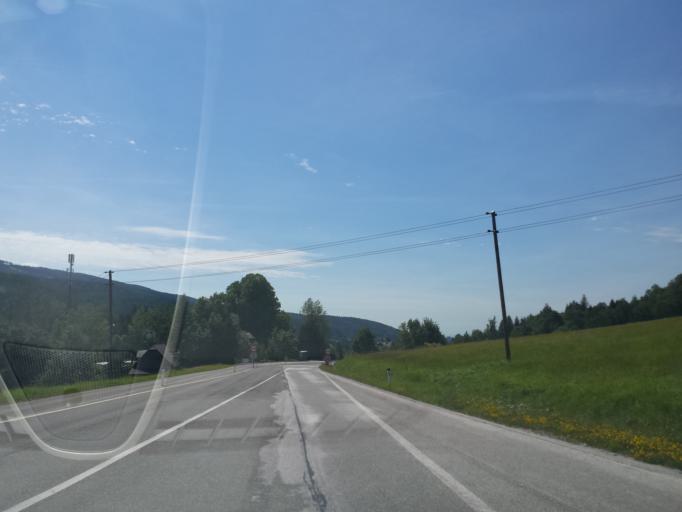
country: AT
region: Lower Austria
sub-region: Politischer Bezirk Neunkirchen
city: Semmering
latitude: 47.6244
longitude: 15.7908
